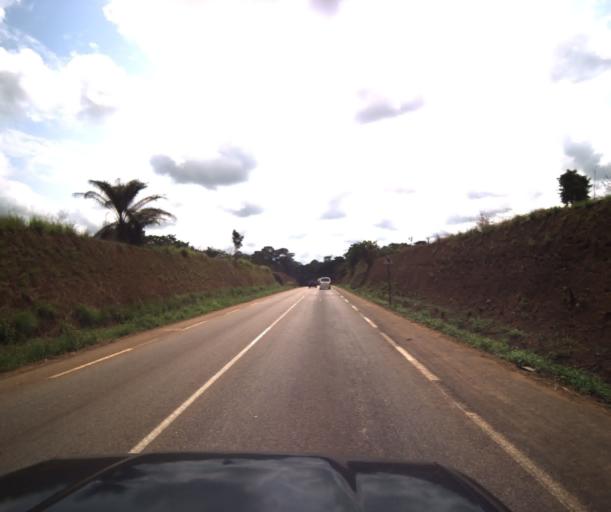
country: CM
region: Centre
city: Eseka
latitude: 3.8561
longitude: 10.5754
